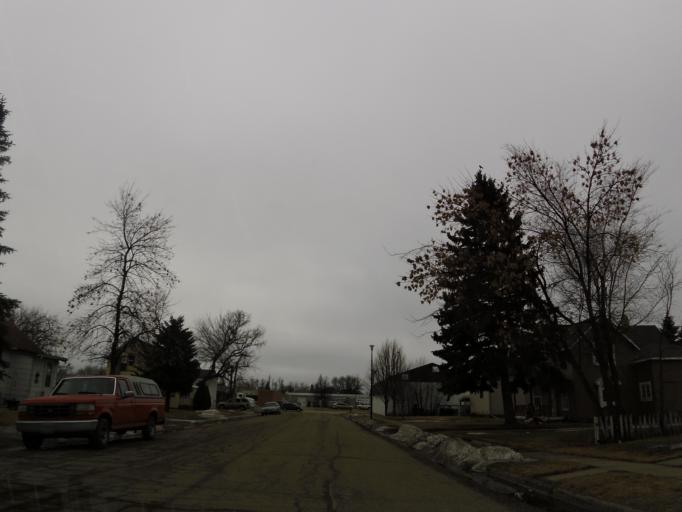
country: US
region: North Dakota
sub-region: Walsh County
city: Grafton
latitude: 48.4135
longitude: -97.4202
